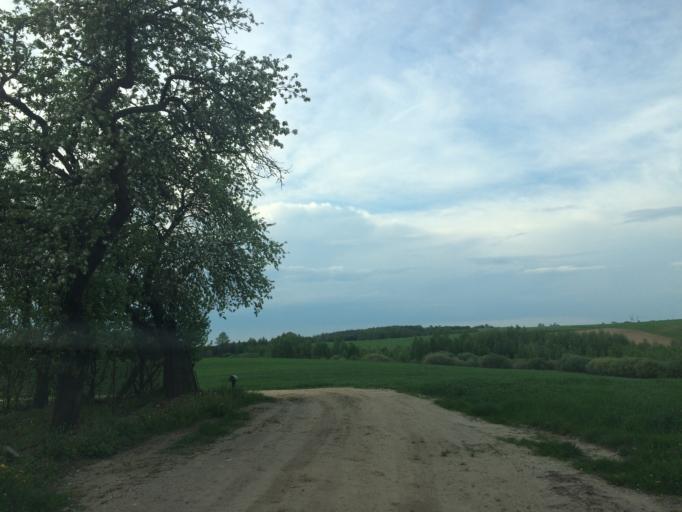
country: PL
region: Kujawsko-Pomorskie
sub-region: Powiat brodnicki
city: Brzozie
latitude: 53.3555
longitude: 19.5792
